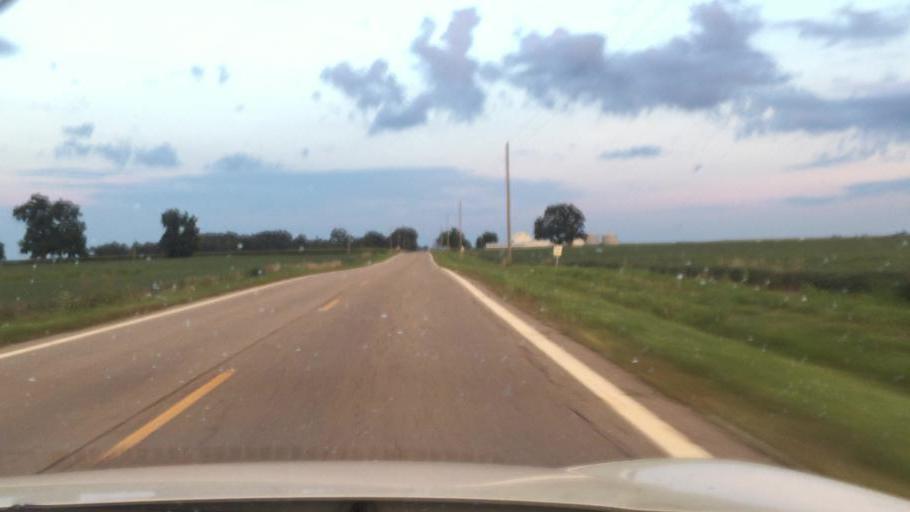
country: US
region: Ohio
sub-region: Madison County
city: Choctaw Lake
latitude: 40.0295
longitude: -83.4870
